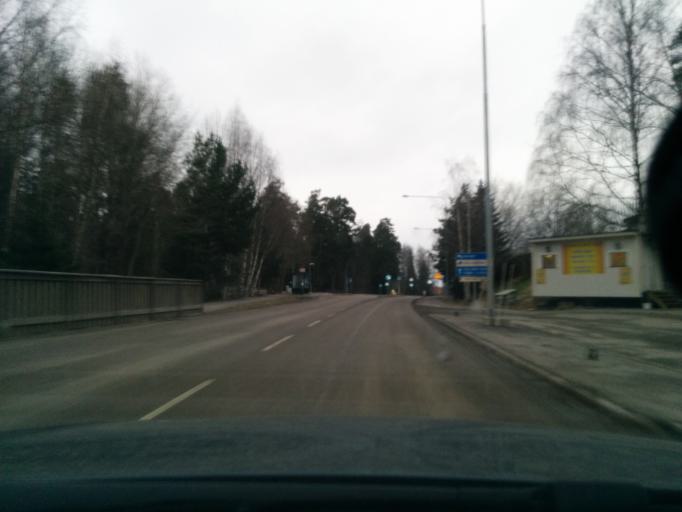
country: SE
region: Stockholm
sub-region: Taby Kommun
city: Taby
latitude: 59.4579
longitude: 18.0351
